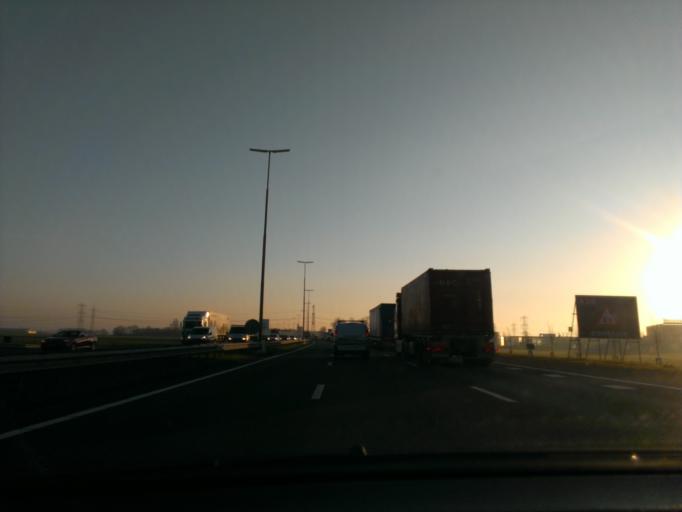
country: NL
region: Overijssel
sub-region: Gemeente Zwolle
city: Zwolle
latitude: 52.5350
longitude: 6.1584
